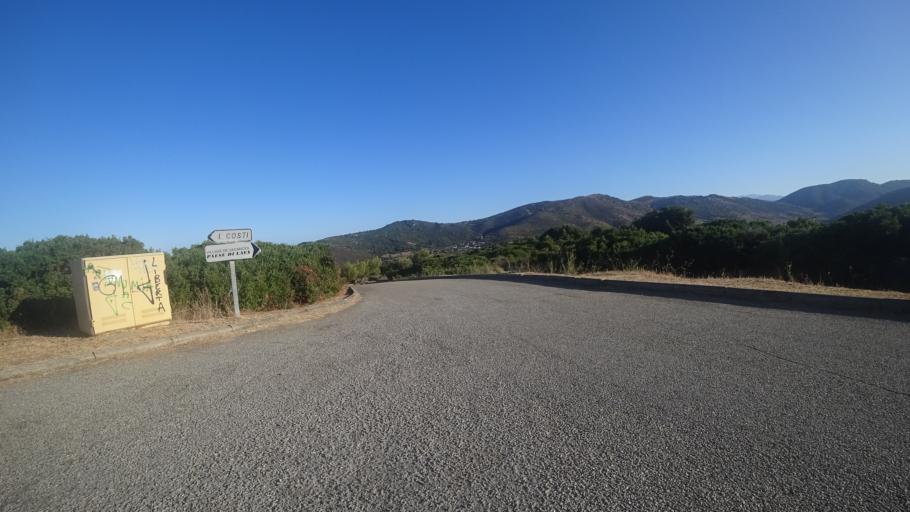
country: FR
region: Corsica
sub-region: Departement de la Corse-du-Sud
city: Alata
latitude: 41.9816
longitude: 8.6760
